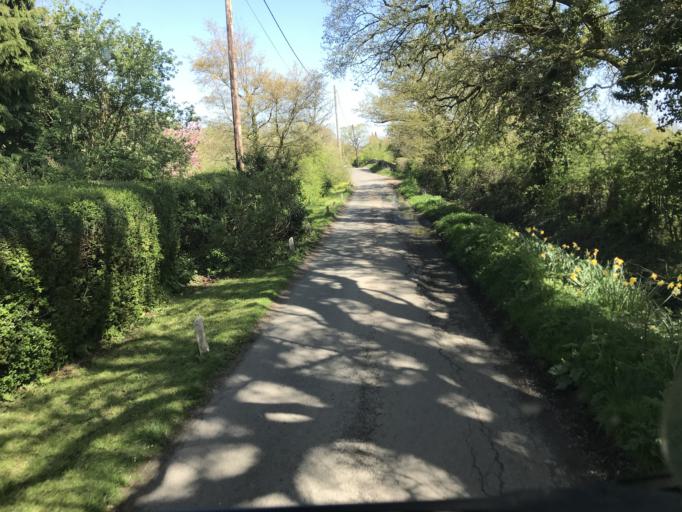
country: GB
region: England
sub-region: Cheshire East
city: Nantwich
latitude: 53.1111
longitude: -2.5208
